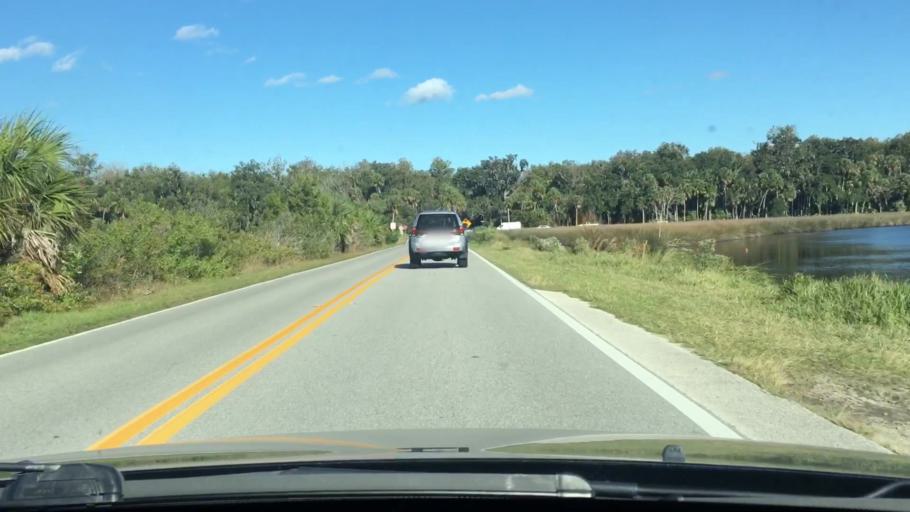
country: US
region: Florida
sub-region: Flagler County
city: Flagler Beach
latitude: 29.4080
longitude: -81.1212
